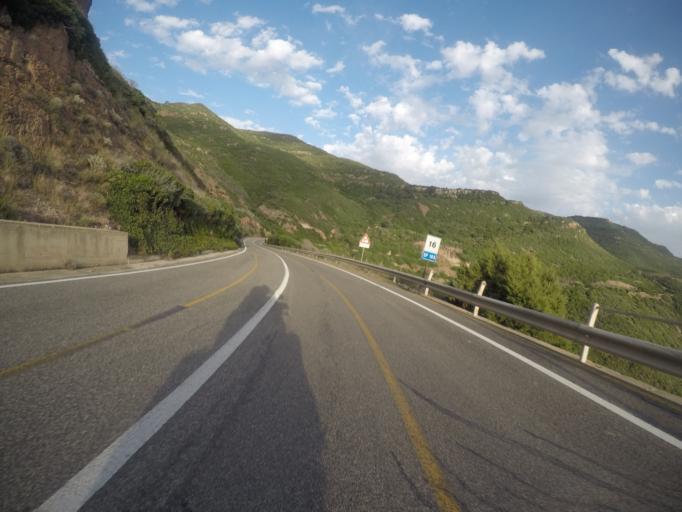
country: IT
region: Sardinia
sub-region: Provincia di Sassari
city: Villanova Monteleone
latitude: 40.4409
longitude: 8.3968
